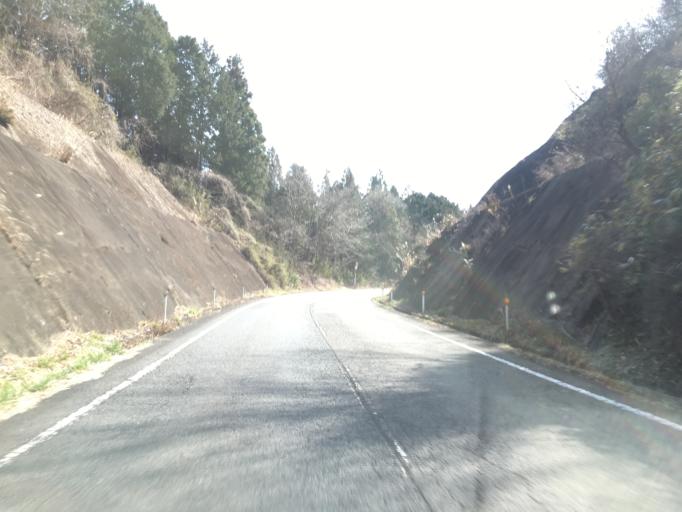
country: JP
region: Ibaraki
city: Daigo
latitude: 36.7873
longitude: 140.4704
